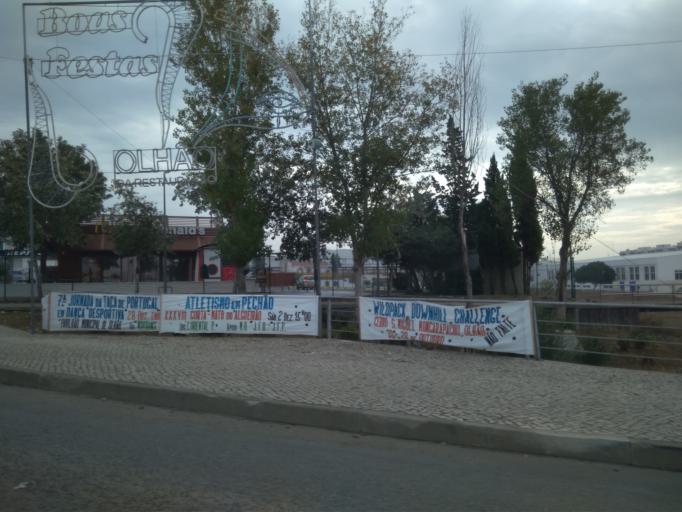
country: PT
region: Faro
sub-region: Olhao
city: Olhao
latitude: 37.0301
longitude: -7.8517
